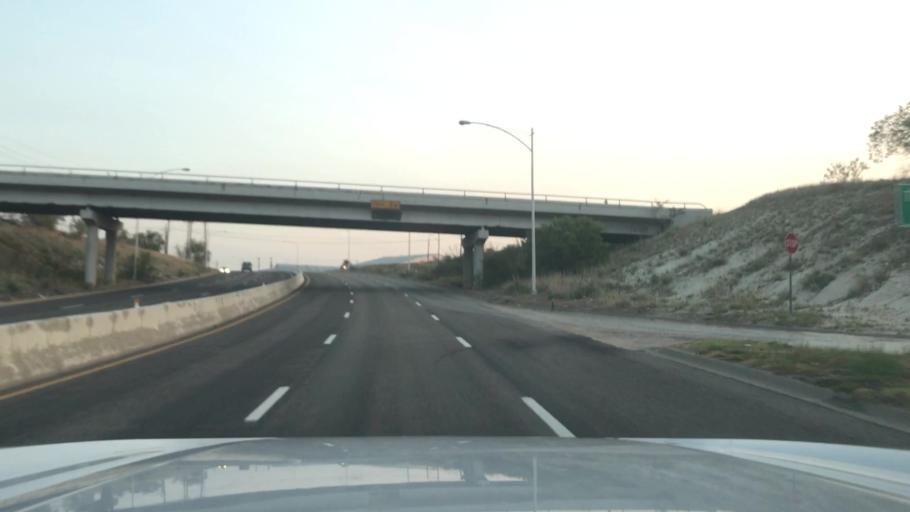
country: US
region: Texas
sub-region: Lubbock County
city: Lubbock
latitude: 33.6030
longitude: -101.8532
